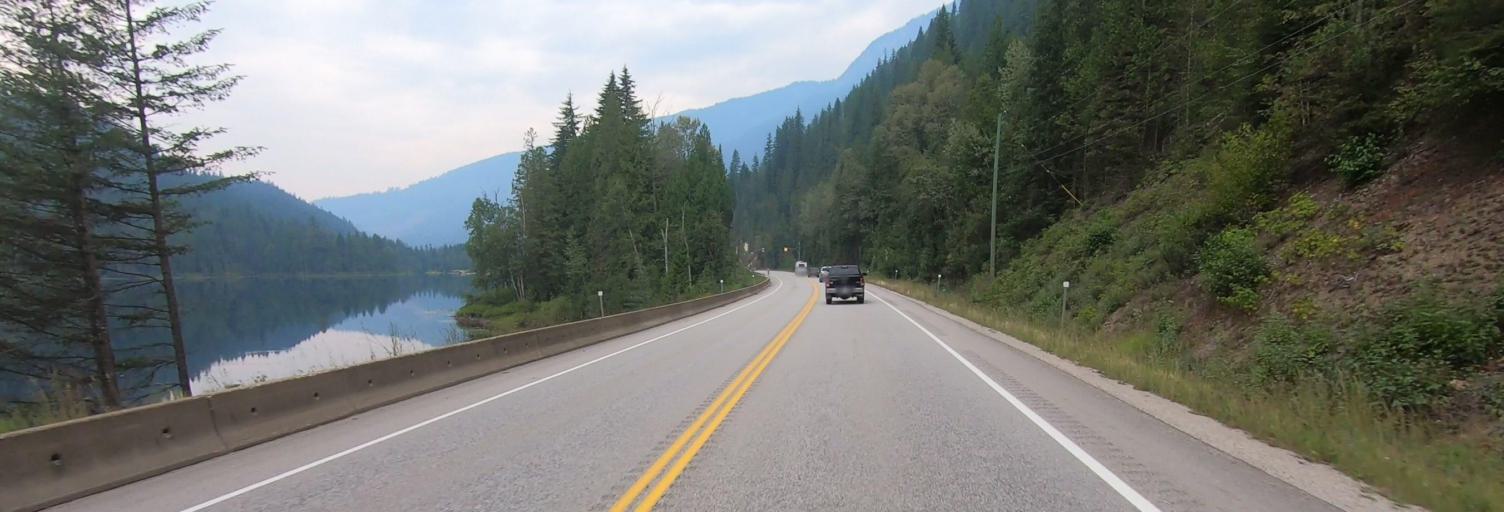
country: CA
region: British Columbia
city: Revelstoke
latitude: 50.9661
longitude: -118.5046
